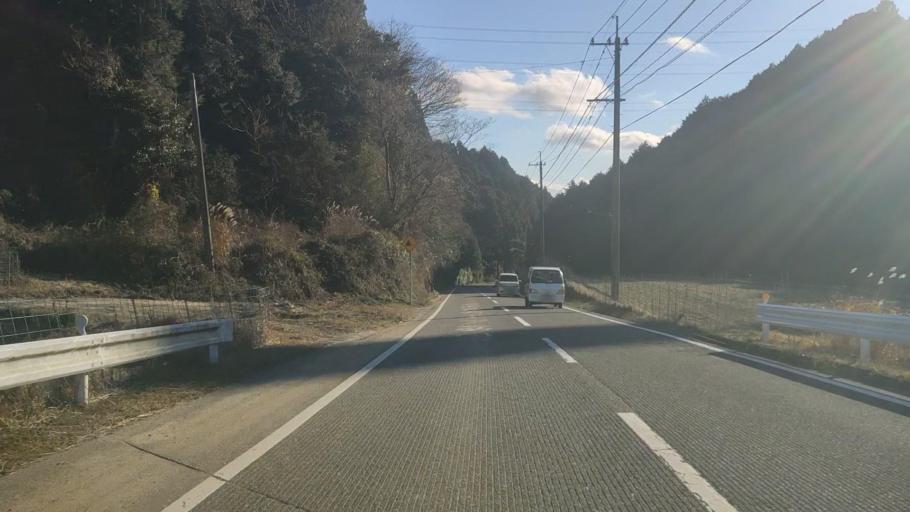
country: JP
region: Saga Prefecture
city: Kanzakimachi-kanzaki
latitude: 33.3988
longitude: 130.2716
